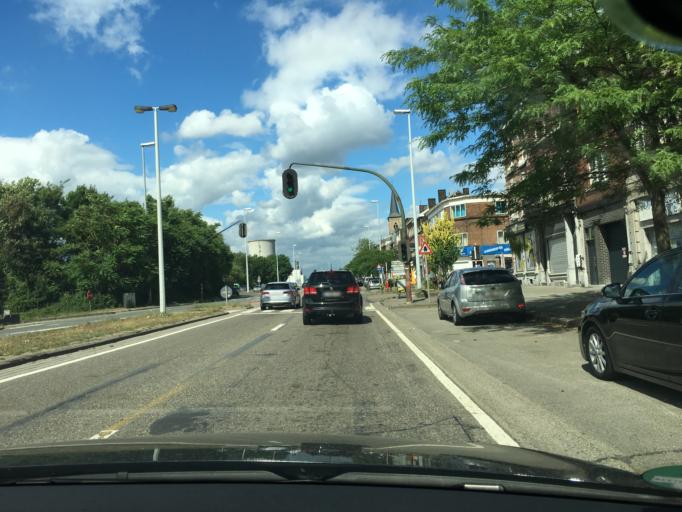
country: BE
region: Wallonia
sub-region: Province de Liege
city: Seraing
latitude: 50.5950
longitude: 5.4823
